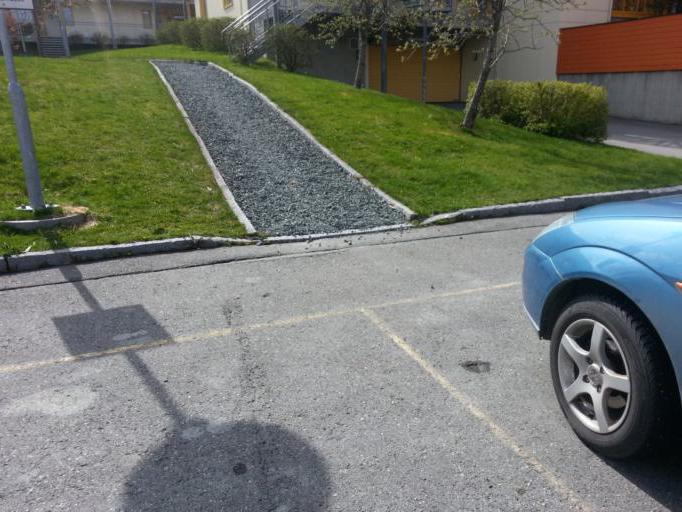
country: NO
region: Sor-Trondelag
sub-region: Trondheim
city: Trondheim
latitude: 63.3956
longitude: 10.3464
